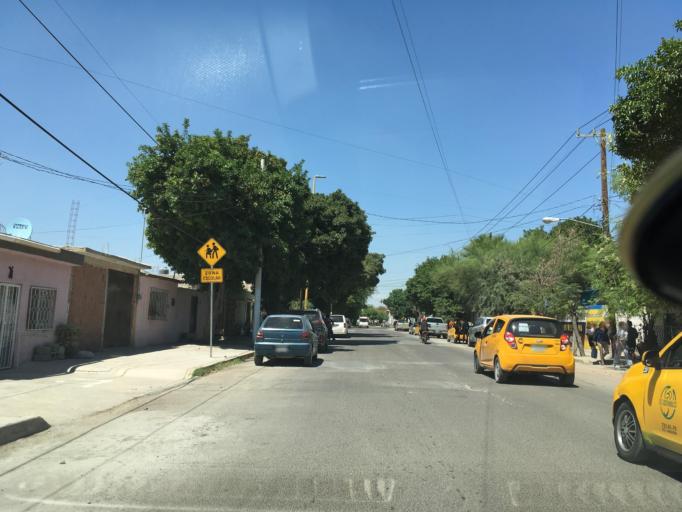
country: MX
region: Coahuila
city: Torreon
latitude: 25.5134
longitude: -103.4320
